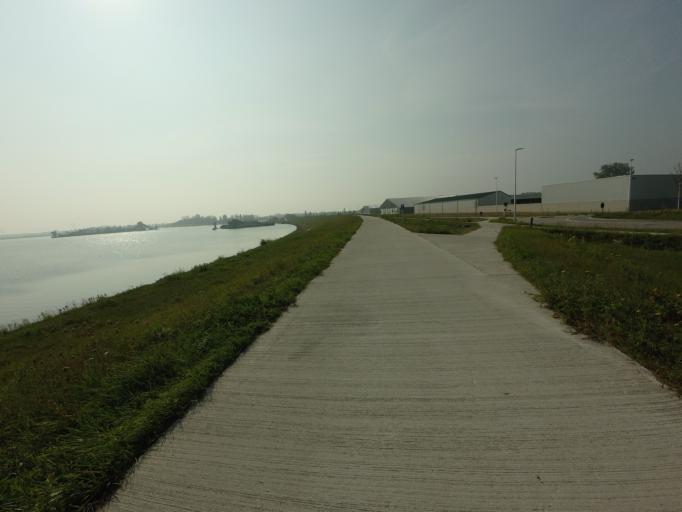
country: BE
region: Flanders
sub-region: Provincie Limburg
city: Maaseik
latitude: 51.1408
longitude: 5.8200
